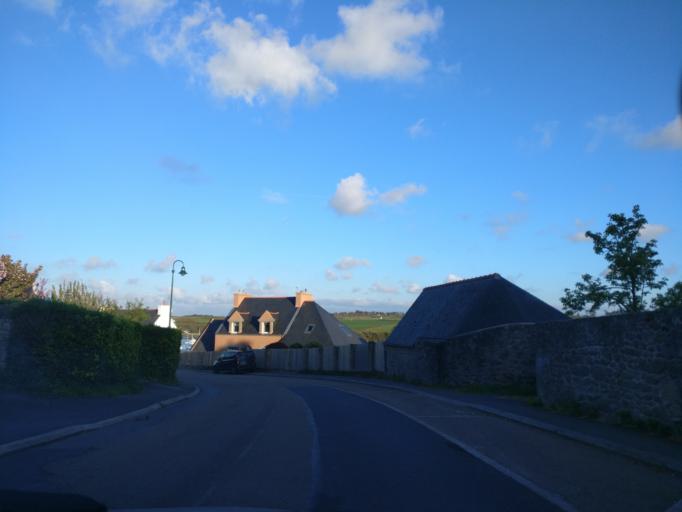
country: FR
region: Brittany
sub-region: Departement du Finistere
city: Lampaul-Plouarzel
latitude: 48.4734
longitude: -4.7550
